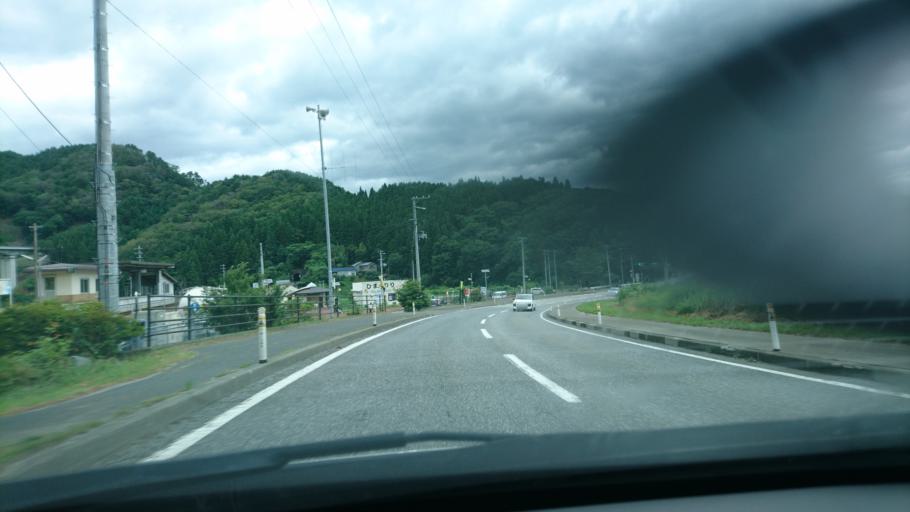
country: JP
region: Iwate
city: Kamaishi
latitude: 39.2014
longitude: 141.8614
